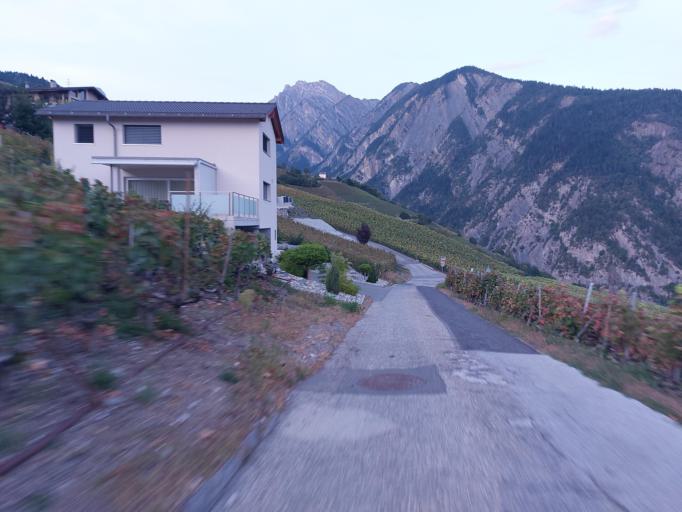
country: CH
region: Valais
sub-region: Conthey District
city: Conthey
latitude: 46.2534
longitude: 7.3067
